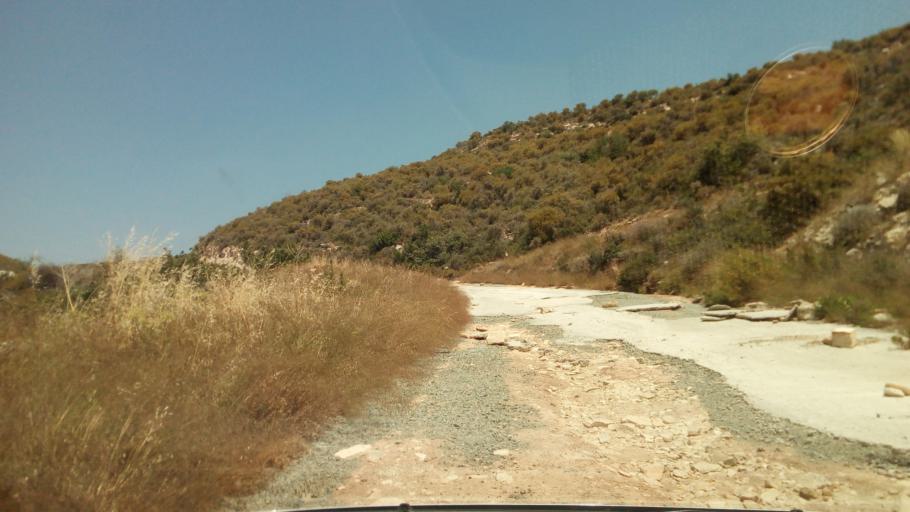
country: CY
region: Limassol
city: Ypsonas
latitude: 34.7300
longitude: 32.9568
